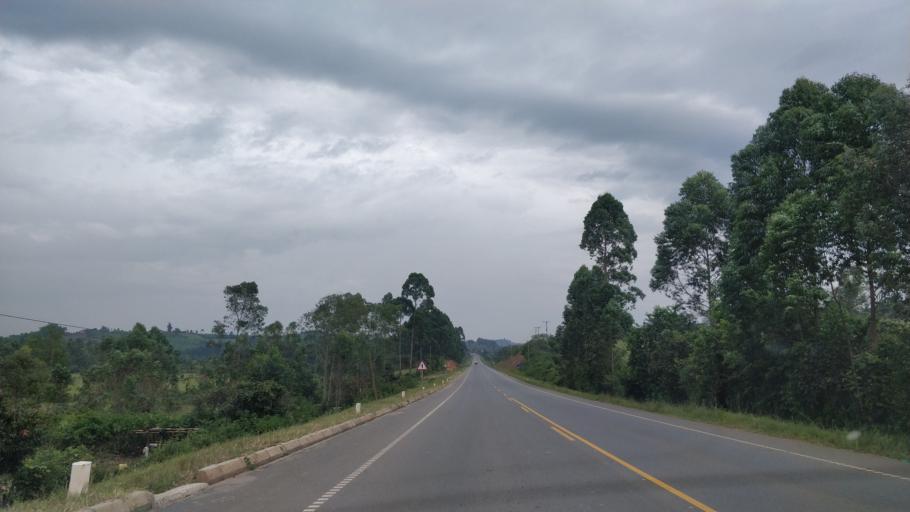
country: UG
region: Western Region
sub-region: Sheema District
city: Kibingo
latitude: -0.6582
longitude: 30.4685
